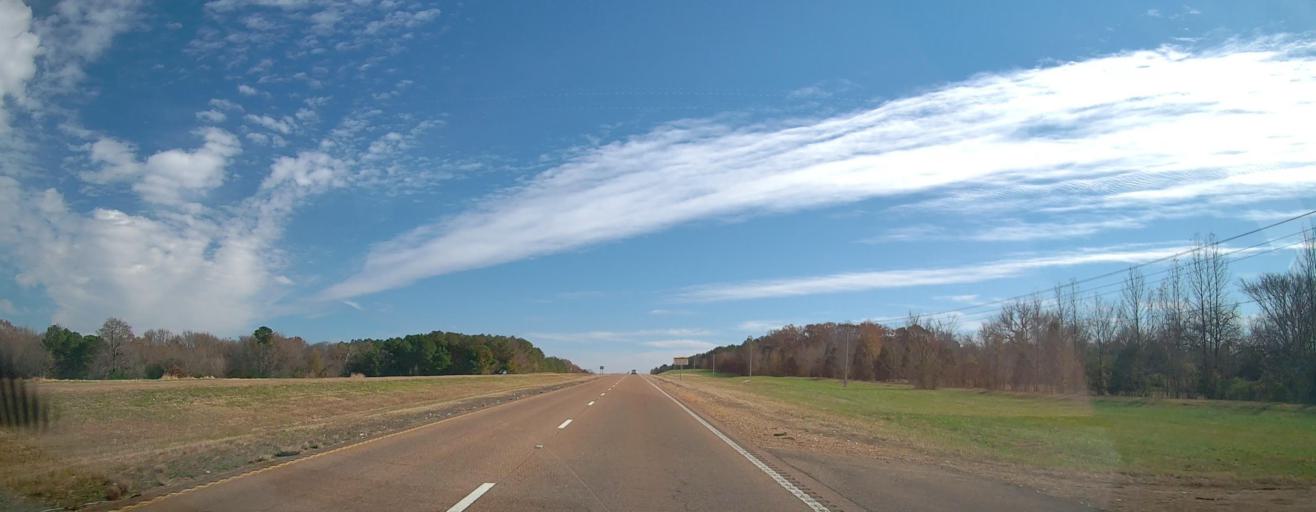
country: US
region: Tennessee
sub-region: Fayette County
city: Piperton
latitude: 34.9569
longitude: -89.5071
